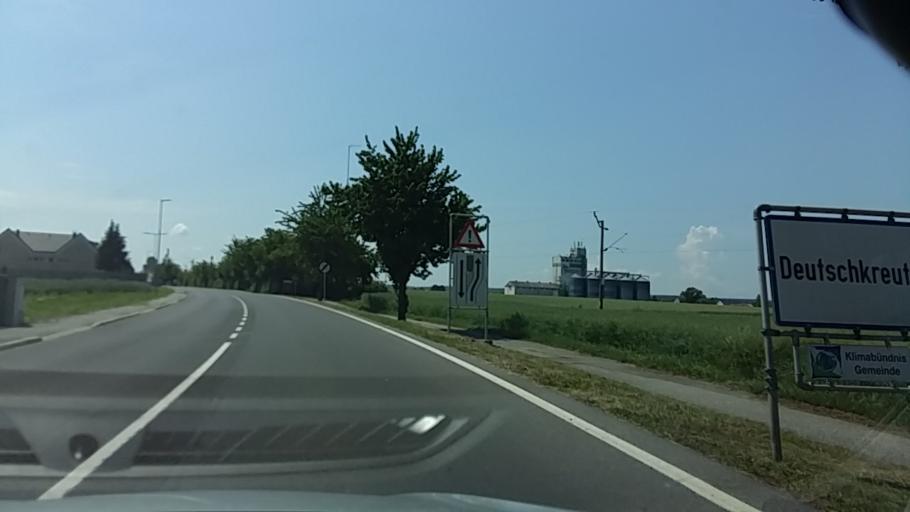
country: AT
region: Burgenland
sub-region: Politischer Bezirk Oberpullendorf
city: Deutschkreutz
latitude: 47.6084
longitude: 16.6247
